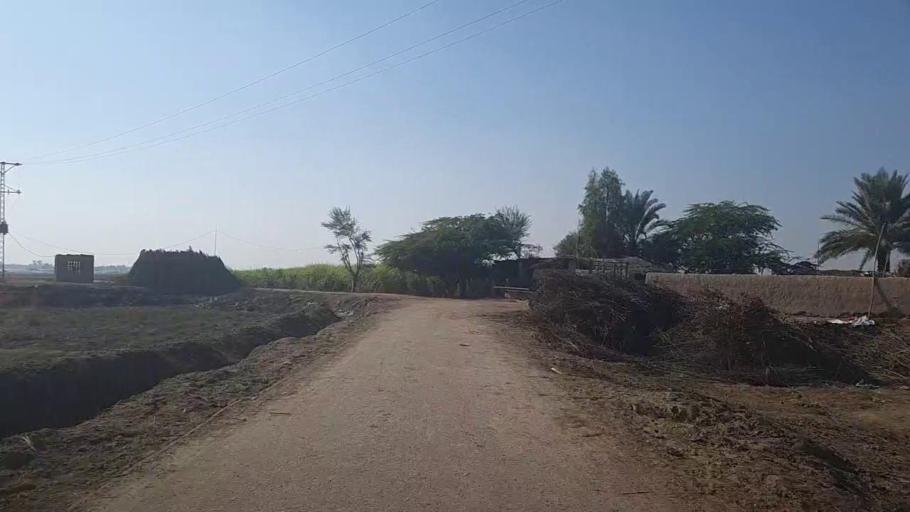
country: PK
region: Sindh
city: Khairpur
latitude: 27.4410
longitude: 68.7295
